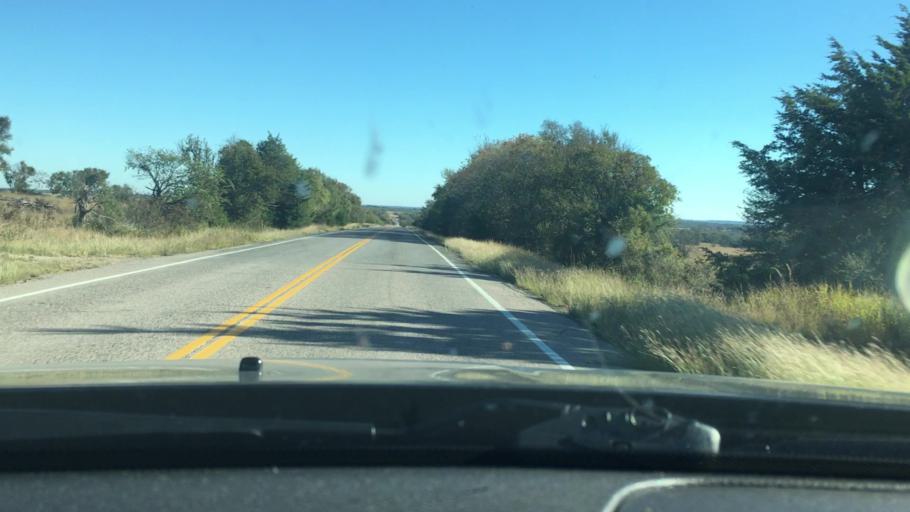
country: US
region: Oklahoma
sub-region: Marshall County
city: Madill
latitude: 34.1387
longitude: -96.7130
